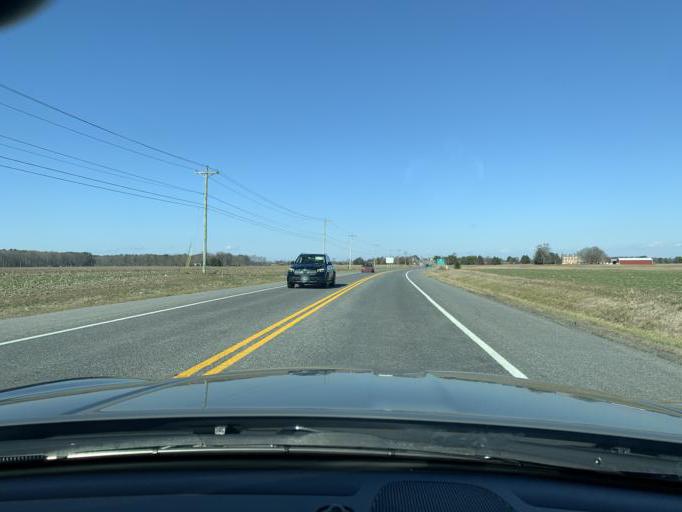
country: US
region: Maryland
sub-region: Queen Anne's County
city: Centreville
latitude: 39.0055
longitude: -76.0746
